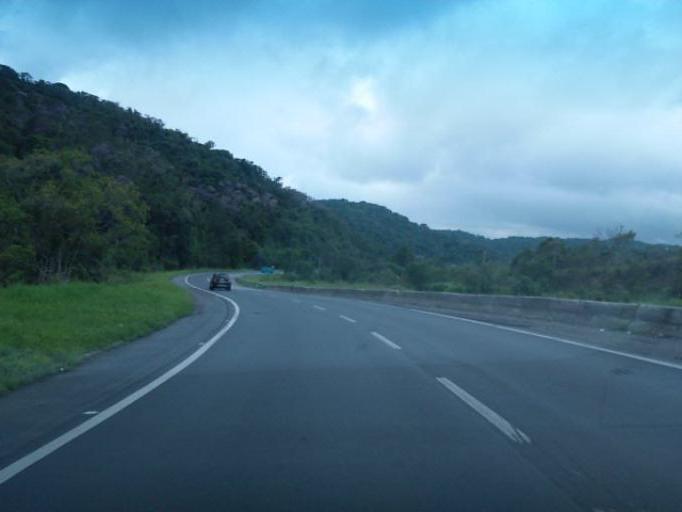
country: BR
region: Sao Paulo
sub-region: Cajati
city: Cajati
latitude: -24.9641
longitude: -48.4246
